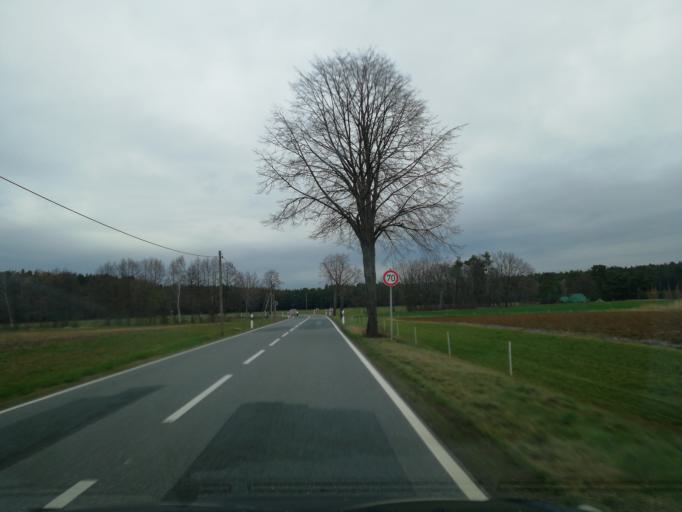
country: DE
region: Brandenburg
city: Vetschau
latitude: 51.7334
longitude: 14.0552
